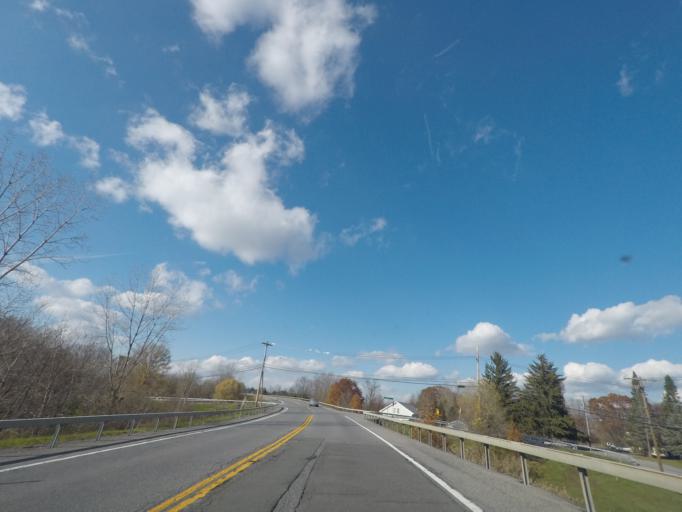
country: US
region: New York
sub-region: Saratoga County
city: Country Knolls
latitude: 42.8911
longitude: -73.8217
